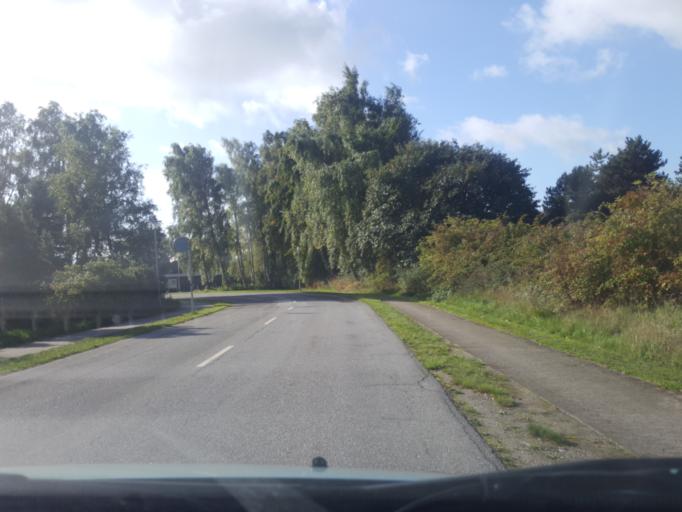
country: DK
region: Zealand
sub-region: Guldborgsund Kommune
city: Nykobing Falster
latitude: 54.6704
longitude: 11.9558
